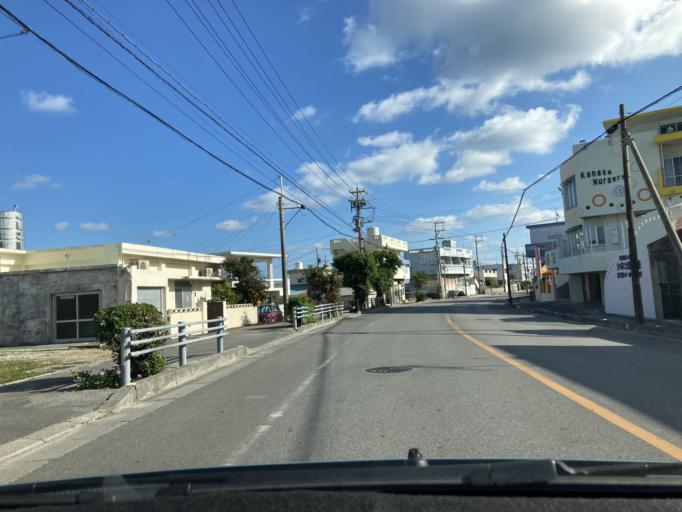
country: JP
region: Okinawa
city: Katsuren-haebaru
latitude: 26.3084
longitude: 127.9128
